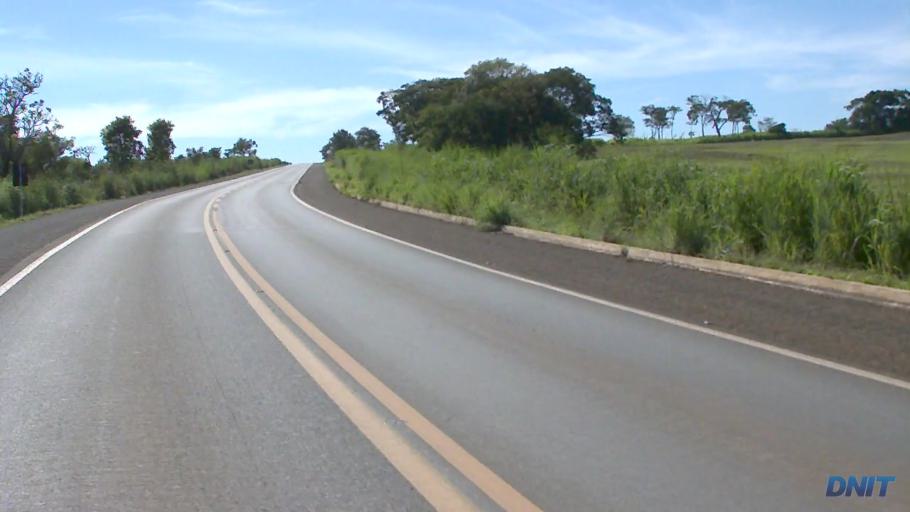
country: BR
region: Goias
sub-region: Padre Bernardo
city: Padre Bernardo
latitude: -15.2100
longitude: -48.4834
